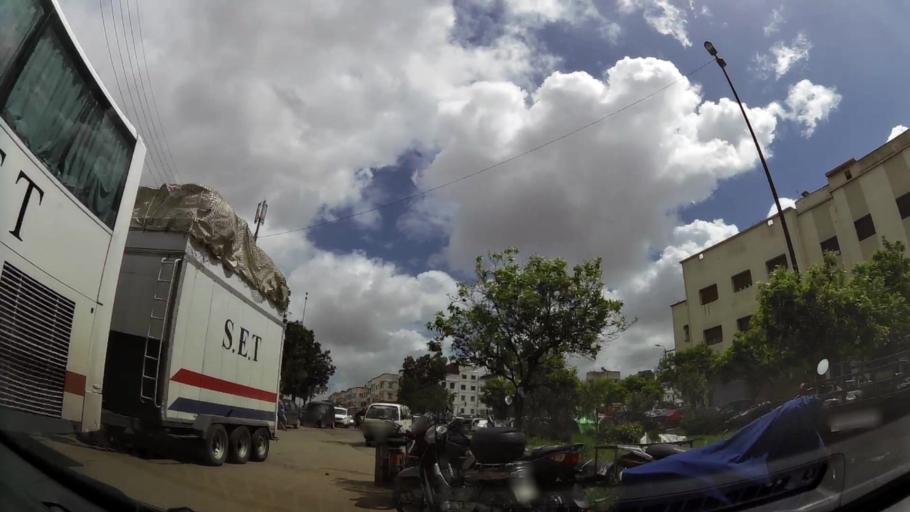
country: MA
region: Grand Casablanca
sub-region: Casablanca
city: Casablanca
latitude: 33.5430
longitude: -7.5822
